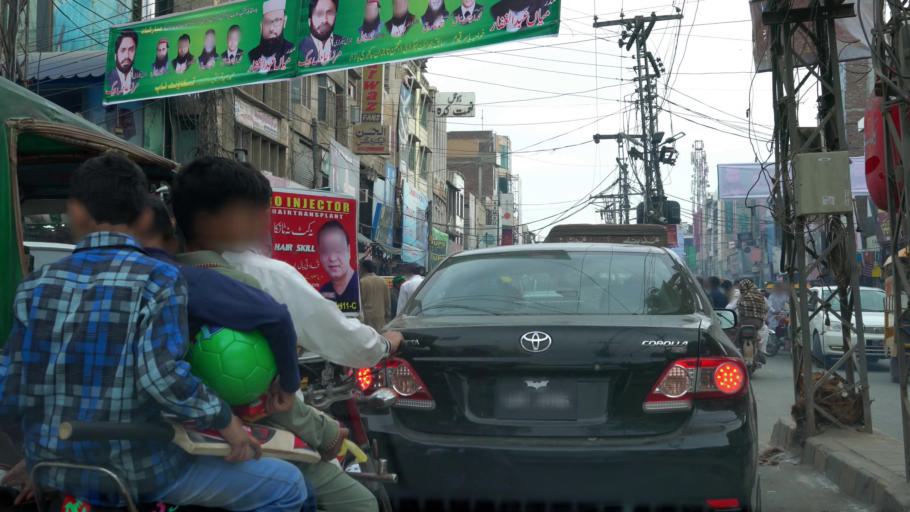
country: PK
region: Punjab
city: Sargodha
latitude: 32.0854
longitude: 72.6644
